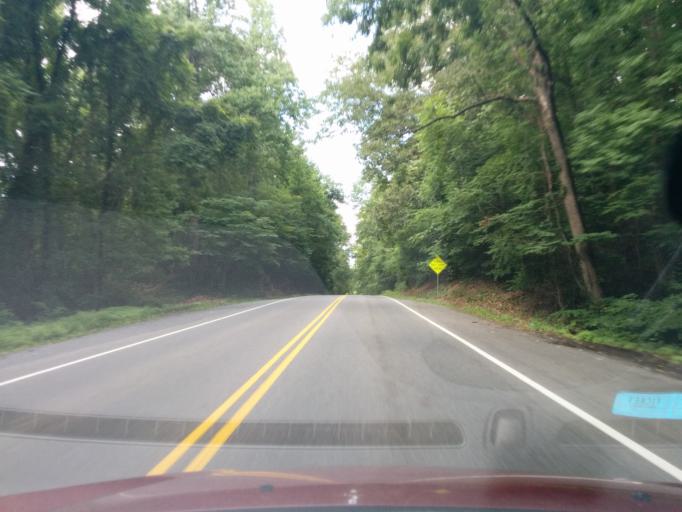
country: US
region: Virginia
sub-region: Rockbridge County
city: Glasgow
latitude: 37.6539
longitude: -79.5196
